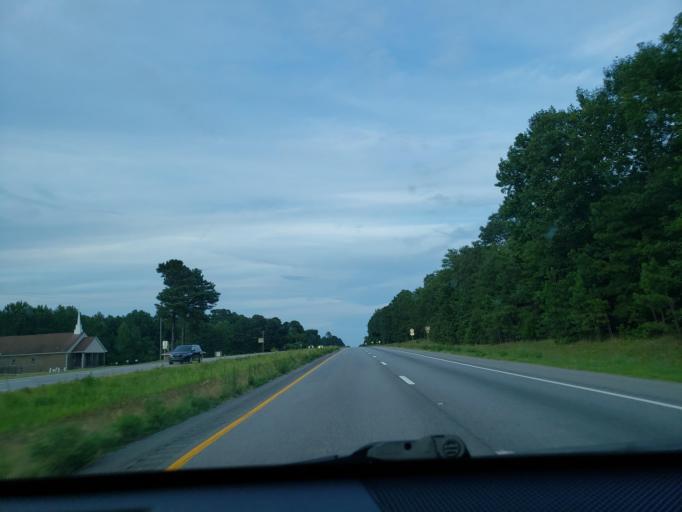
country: US
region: Virginia
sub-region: City of Emporia
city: Emporia
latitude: 36.6947
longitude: -77.3443
